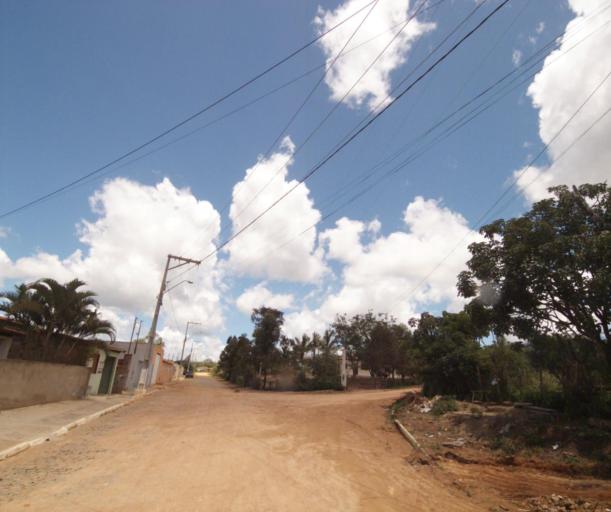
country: BR
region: Bahia
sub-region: Pocoes
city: Pocoes
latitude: -14.3752
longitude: -40.4998
